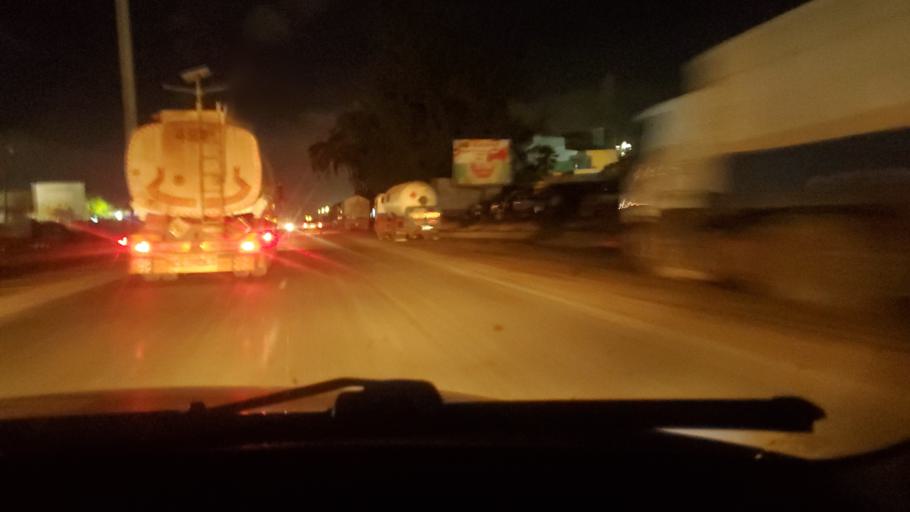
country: SN
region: Dakar
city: Pikine
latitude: 14.7432
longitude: -17.3910
